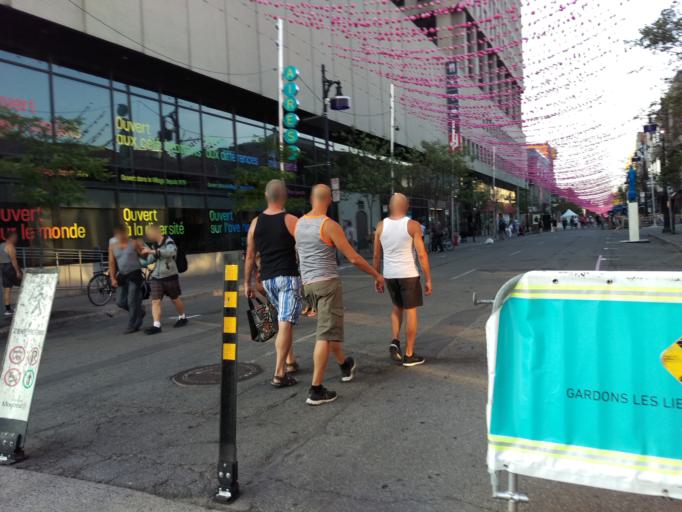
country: CA
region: Quebec
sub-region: Montreal
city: Montreal
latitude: 45.5150
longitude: -73.5589
